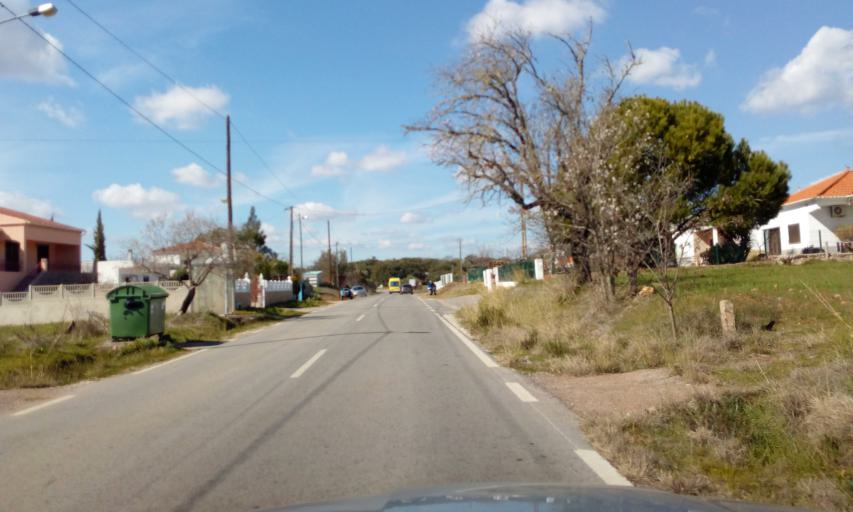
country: PT
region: Faro
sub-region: Loule
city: Loule
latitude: 37.2442
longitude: -8.0565
